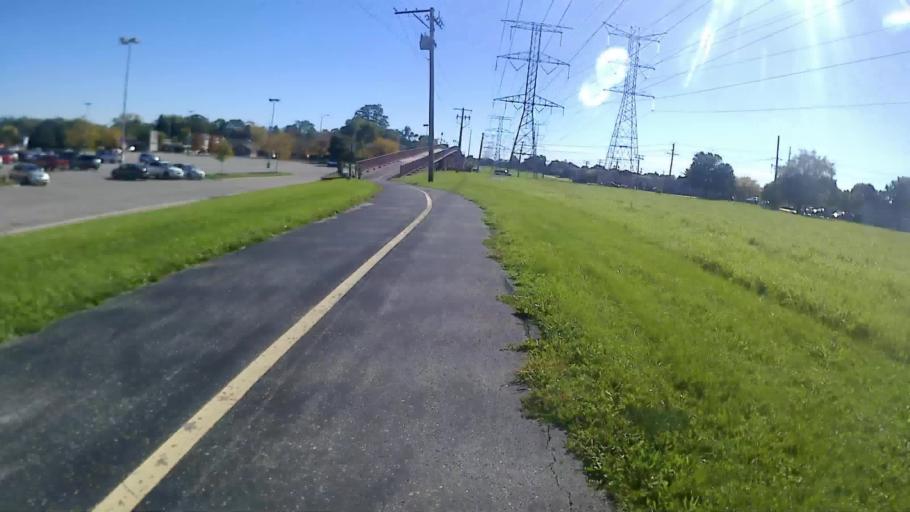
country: US
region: Illinois
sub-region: DuPage County
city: Wood Dale
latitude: 41.9674
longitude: -87.9938
